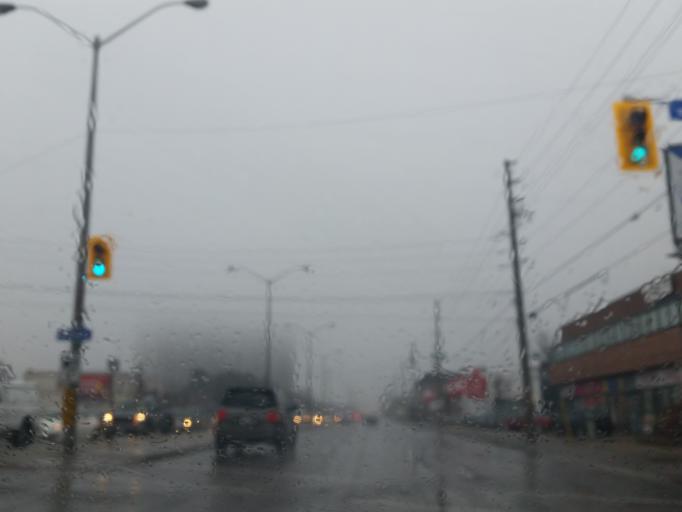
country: CA
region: Ontario
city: Scarborough
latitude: 43.7661
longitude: -79.1911
